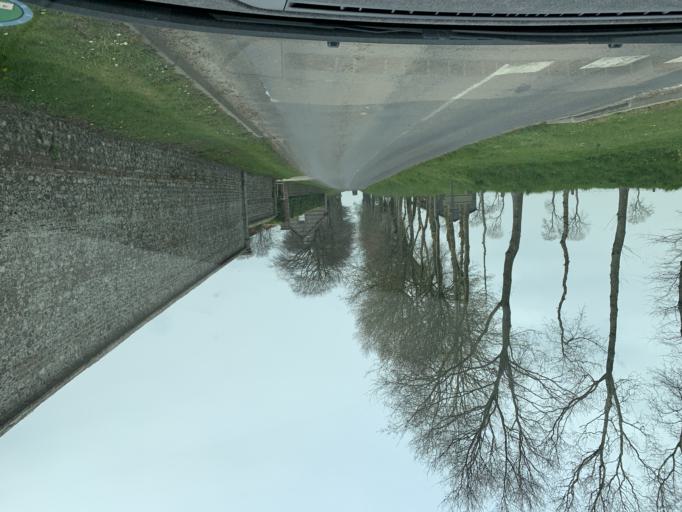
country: FR
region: Haute-Normandie
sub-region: Departement de la Seine-Maritime
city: Saint-Valery-en-Caux
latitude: 49.8562
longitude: 0.7612
